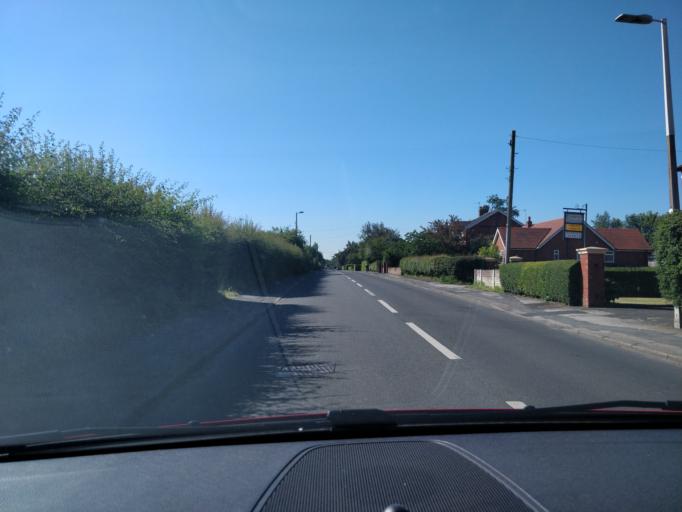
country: GB
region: England
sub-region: Lancashire
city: Tarleton
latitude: 53.7061
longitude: -2.8423
